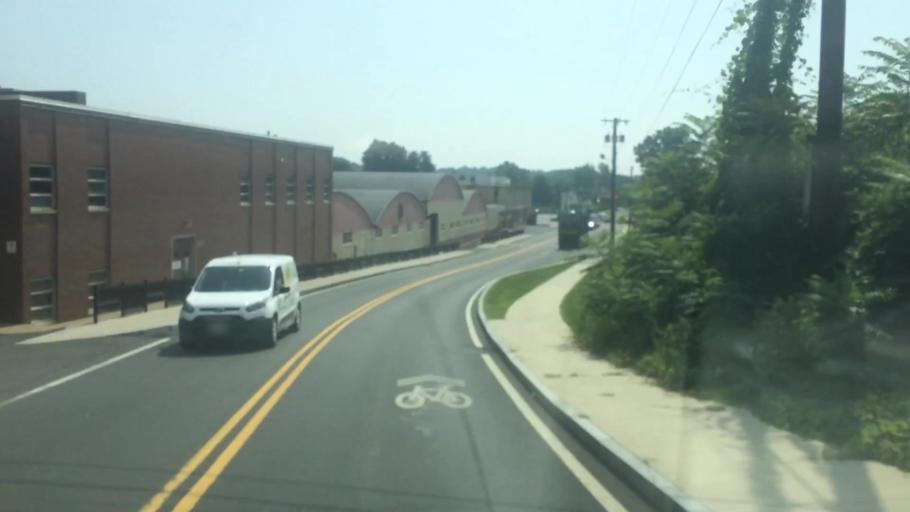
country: US
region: Massachusetts
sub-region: Hampden County
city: Westfield
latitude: 42.1371
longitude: -72.7426
